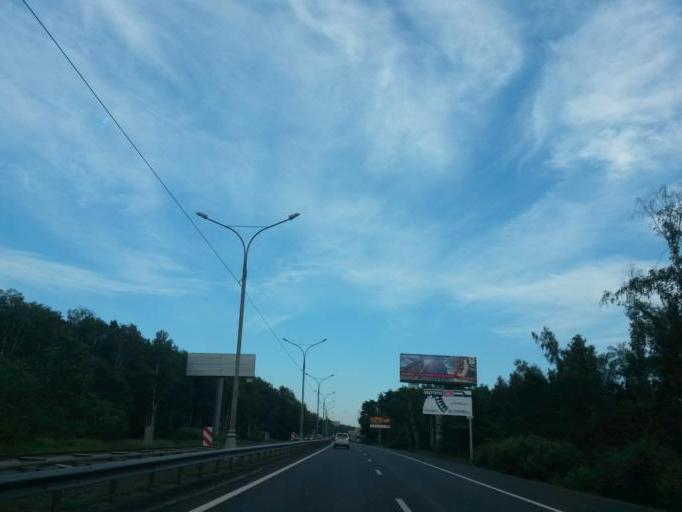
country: RU
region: Moskovskaya
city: Petrovskaya
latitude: 55.5534
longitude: 37.7845
